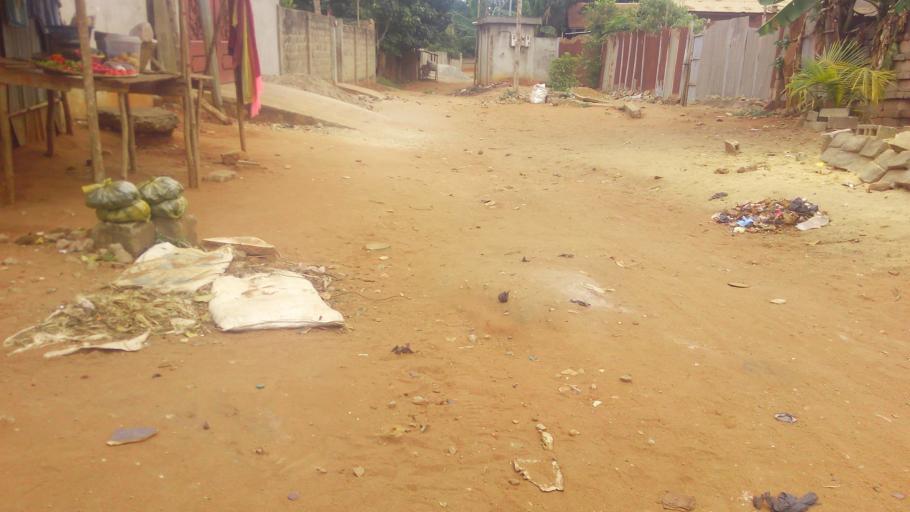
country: BJ
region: Atlantique
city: Abomey-Calavi
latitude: 6.4466
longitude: 2.3430
